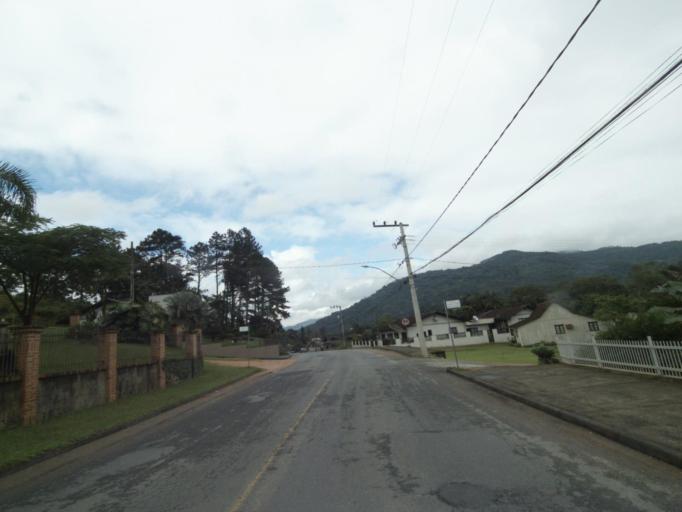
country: BR
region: Santa Catarina
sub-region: Pomerode
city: Pomerode
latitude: -26.7208
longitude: -49.1792
